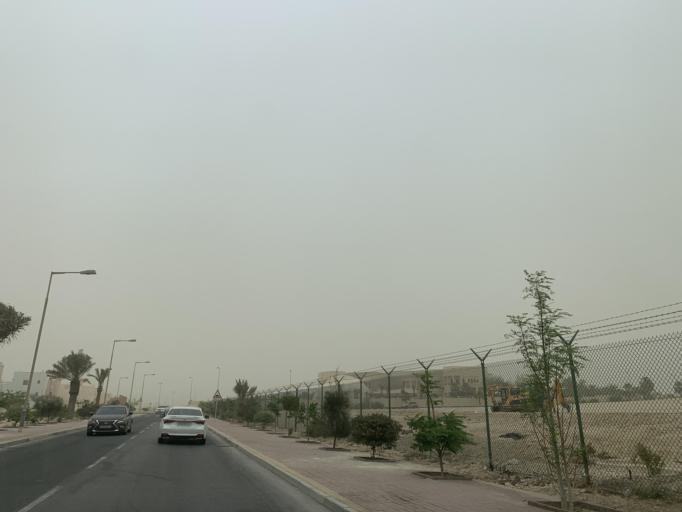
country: BH
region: Central Governorate
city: Madinat Hamad
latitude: 26.1349
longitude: 50.5145
